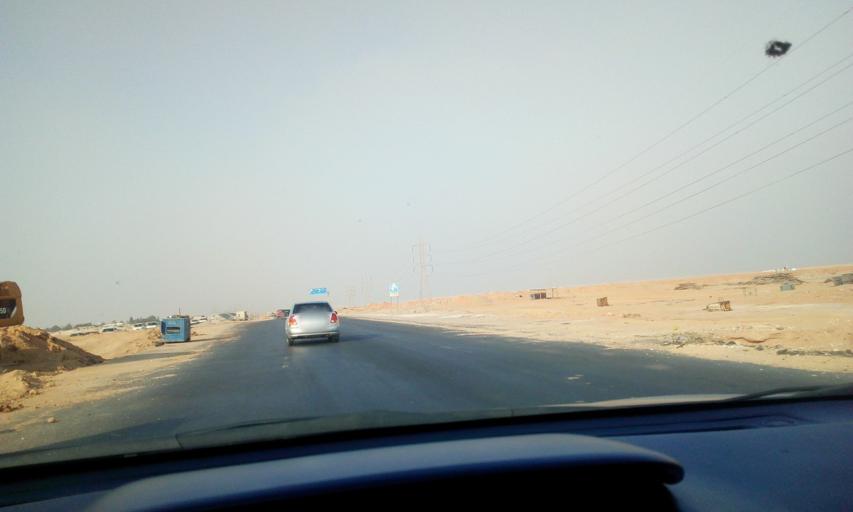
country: EG
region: Al Jizah
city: Madinat Sittah Uktubar
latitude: 29.8667
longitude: 31.0717
